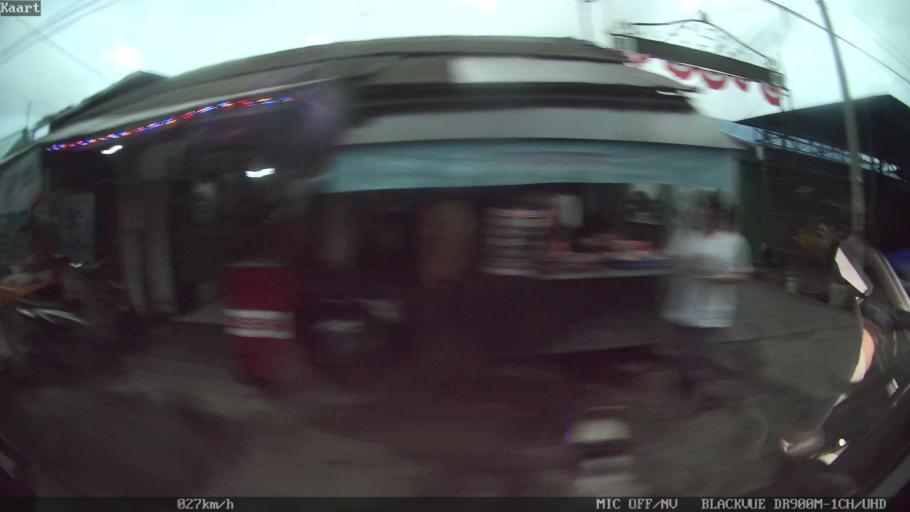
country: ID
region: Bali
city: Banjar Kayangan
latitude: -8.6239
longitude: 115.2240
